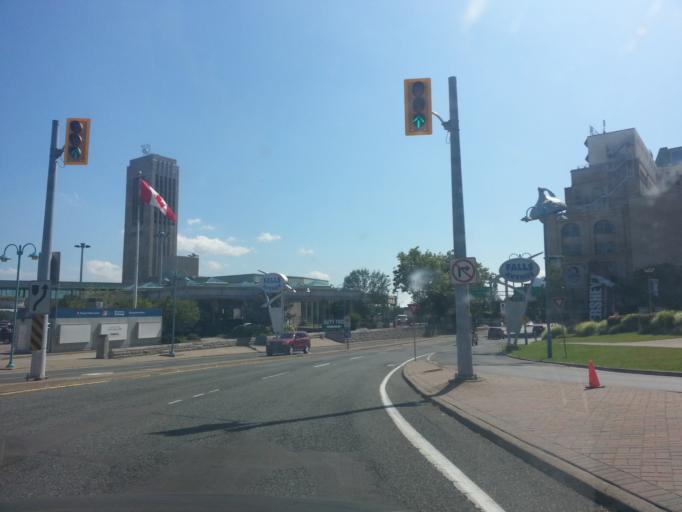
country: CA
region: Ontario
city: Niagara Falls
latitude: 43.0932
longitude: -79.0701
